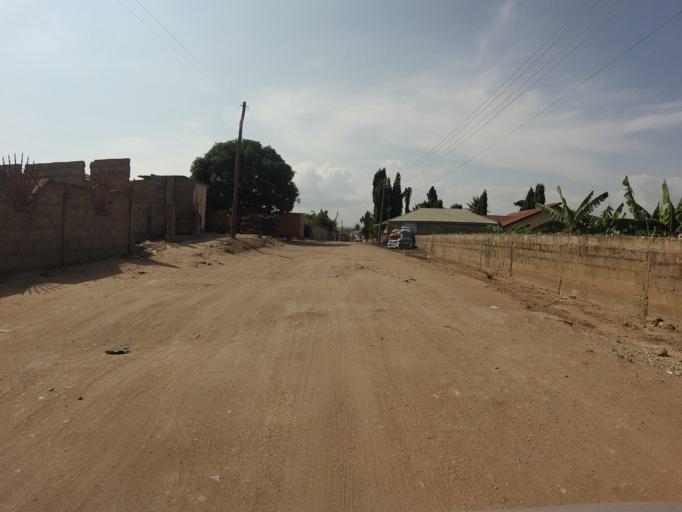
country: GH
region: Greater Accra
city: Dome
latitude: 5.6415
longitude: -0.2344
